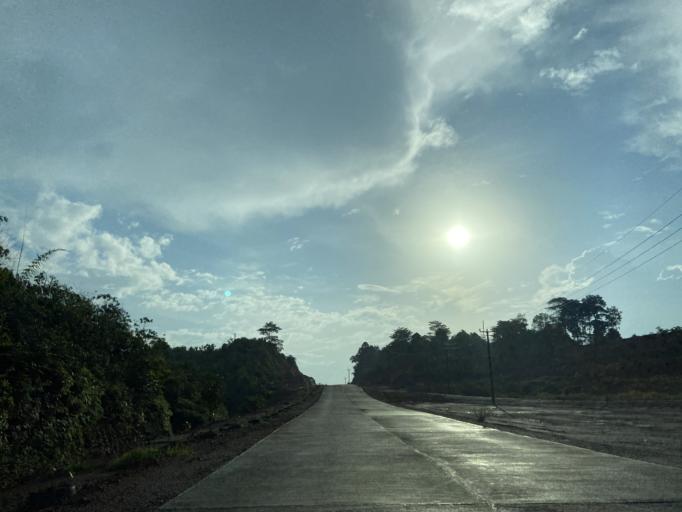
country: ID
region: Riau Islands
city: Tanjungpinang
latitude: 0.8965
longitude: 104.1262
